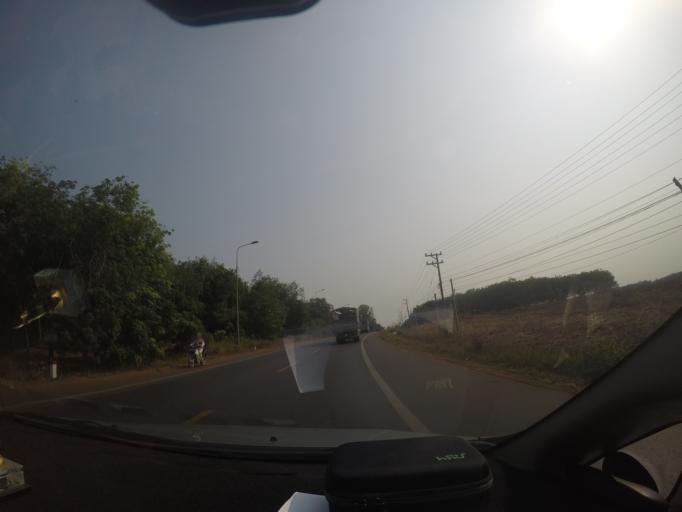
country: VN
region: Dong Nai
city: Vinh An
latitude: 11.1342
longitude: 107.2220
